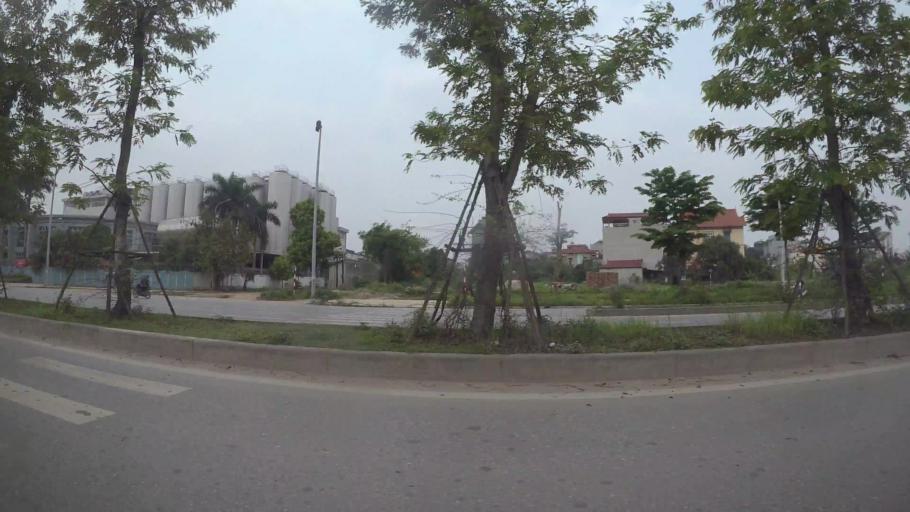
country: VN
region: Ha Noi
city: Cau Dien
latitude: 21.0388
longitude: 105.7437
